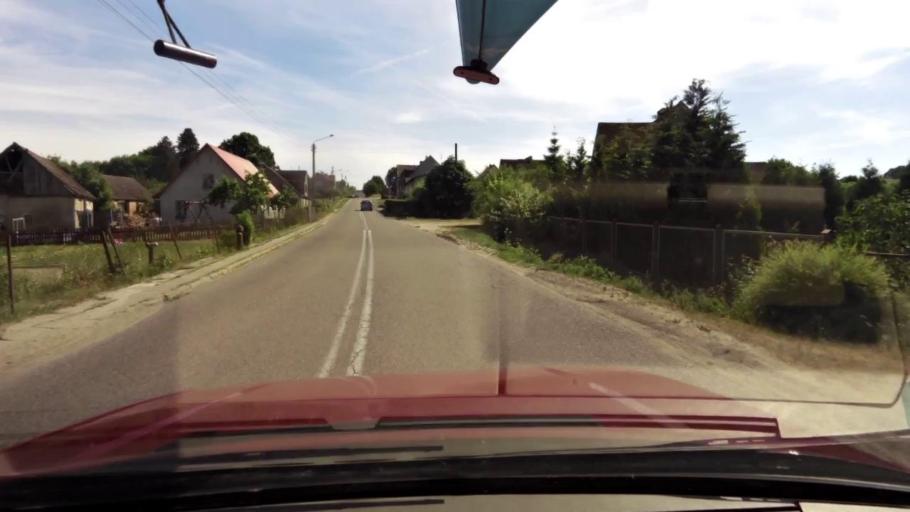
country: PL
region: Pomeranian Voivodeship
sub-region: Powiat slupski
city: Kepice
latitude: 54.2749
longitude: 16.9597
